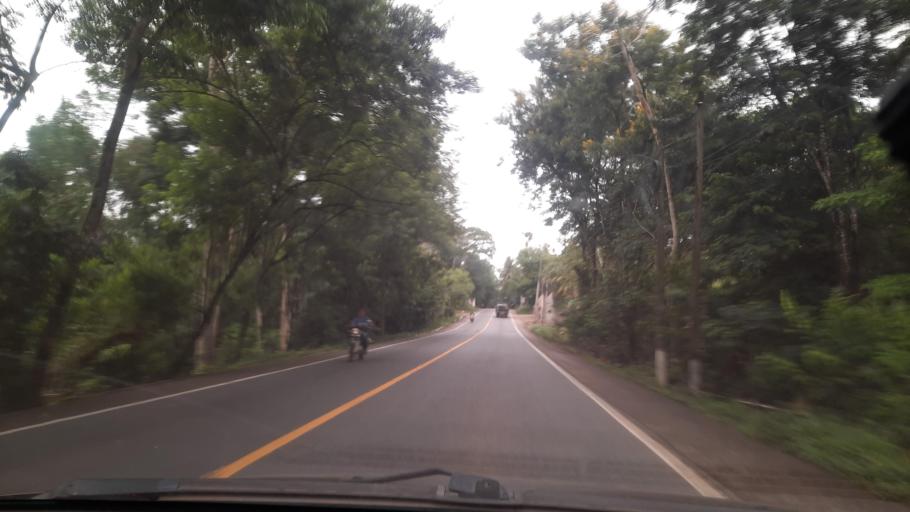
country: GT
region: Izabal
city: Morales
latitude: 15.4404
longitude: -88.9523
